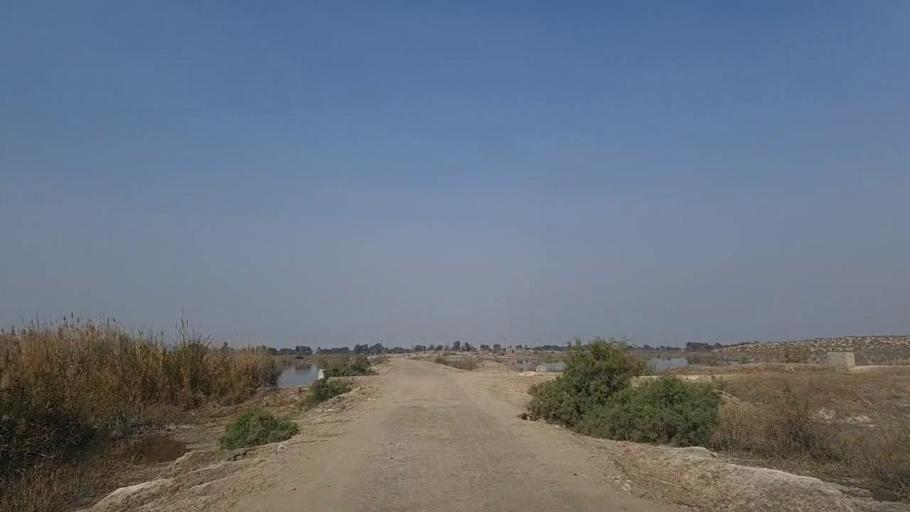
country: PK
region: Sindh
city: Daur
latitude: 26.5070
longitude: 68.4796
